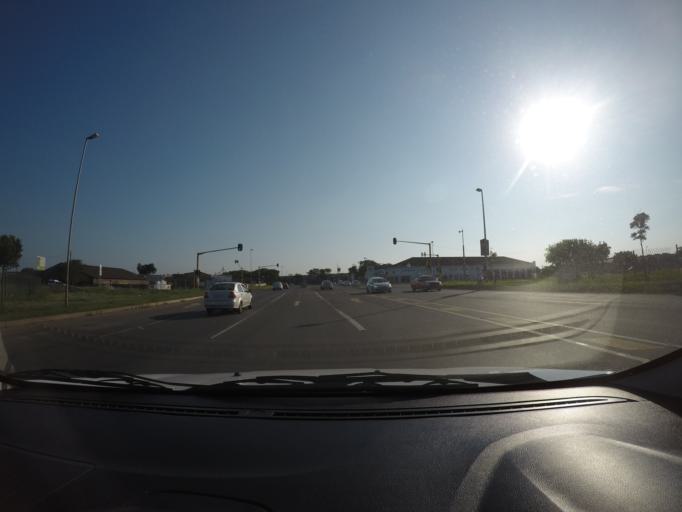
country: ZA
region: KwaZulu-Natal
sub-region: uThungulu District Municipality
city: Richards Bay
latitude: -28.7537
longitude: 32.0259
